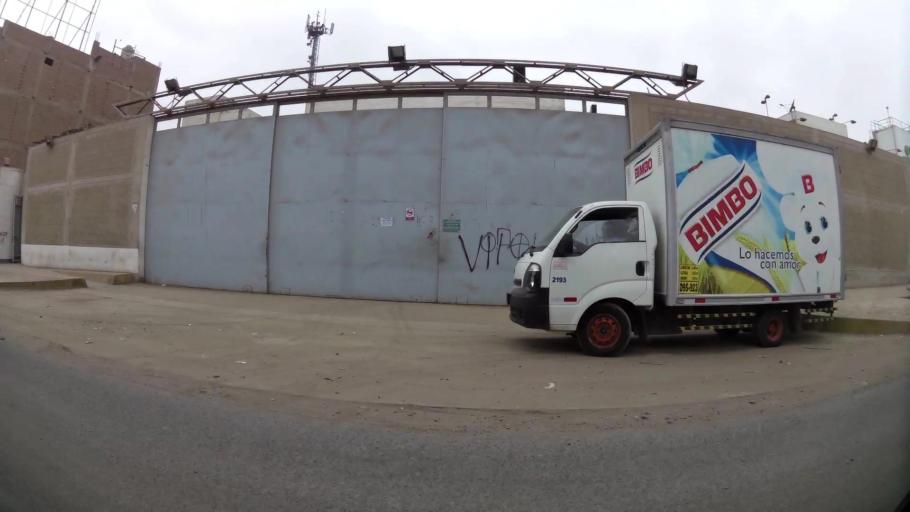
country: PE
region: Lima
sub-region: Lima
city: Independencia
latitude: -11.9551
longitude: -77.0860
